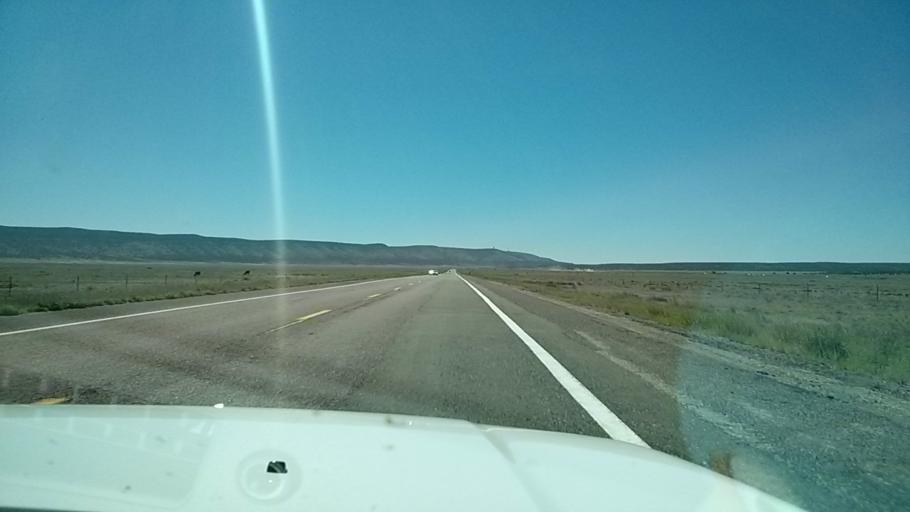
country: US
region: Arizona
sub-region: Mohave County
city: Peach Springs
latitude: 35.4132
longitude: -113.0356
